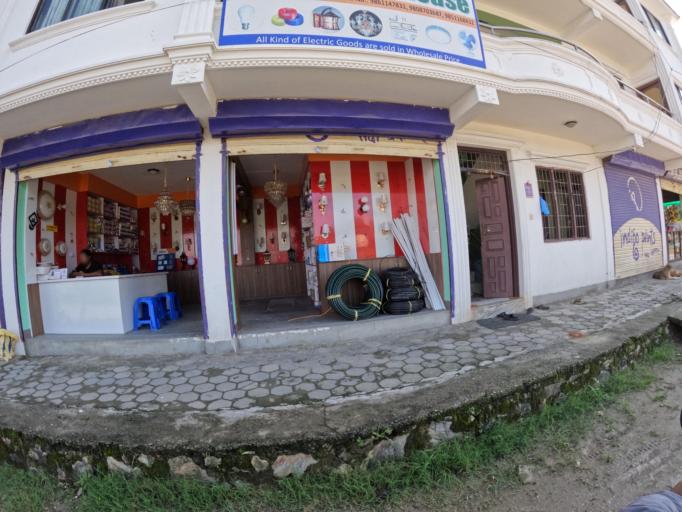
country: NP
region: Central Region
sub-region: Bagmati Zone
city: Kathmandu
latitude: 27.7588
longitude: 85.3358
